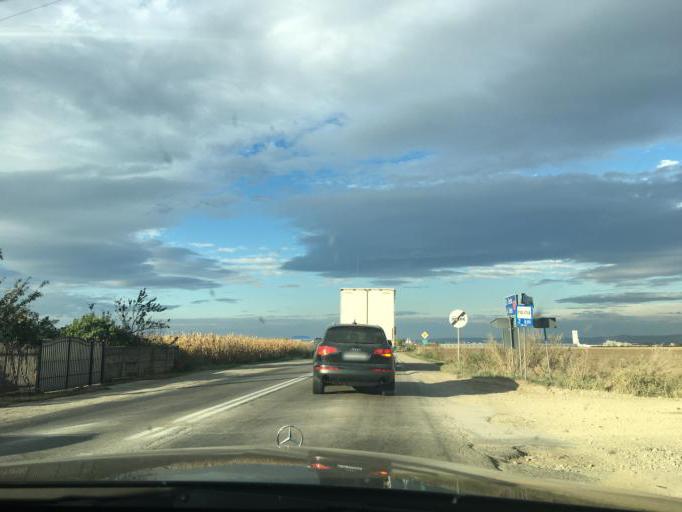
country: RO
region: Alba
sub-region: Oras Teius
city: Teius
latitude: 46.1772
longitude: 23.6549
